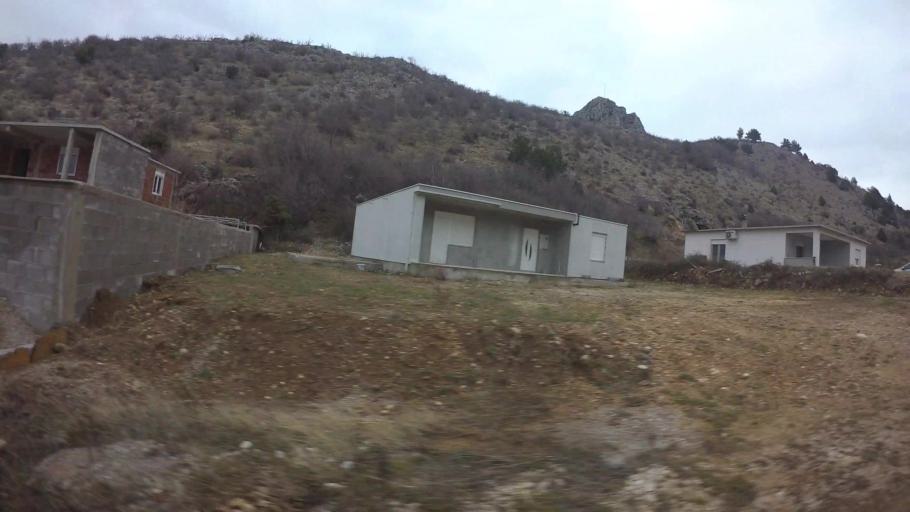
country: BA
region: Federation of Bosnia and Herzegovina
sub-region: Hercegovacko-Bosanski Kanton
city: Mostar
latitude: 43.3611
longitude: 17.8232
